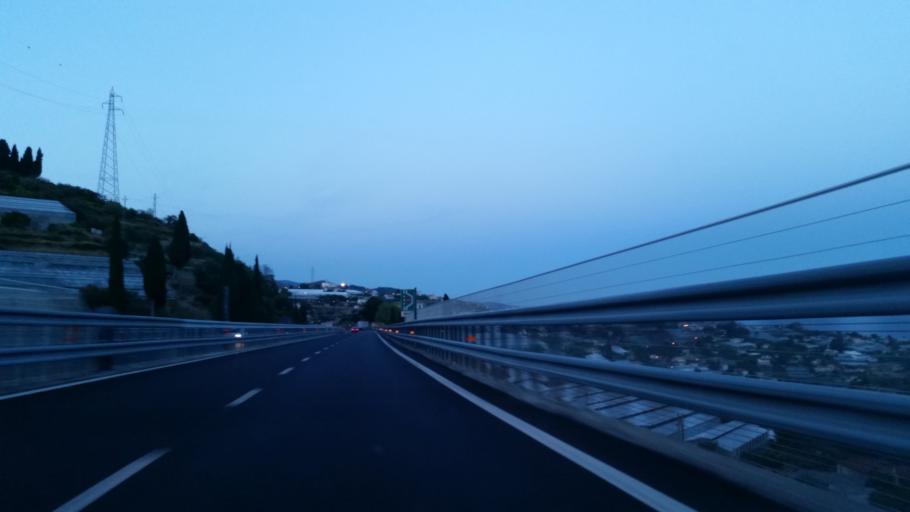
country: IT
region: Liguria
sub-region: Provincia di Imperia
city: Ospedaletti
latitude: 43.8230
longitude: 7.7383
